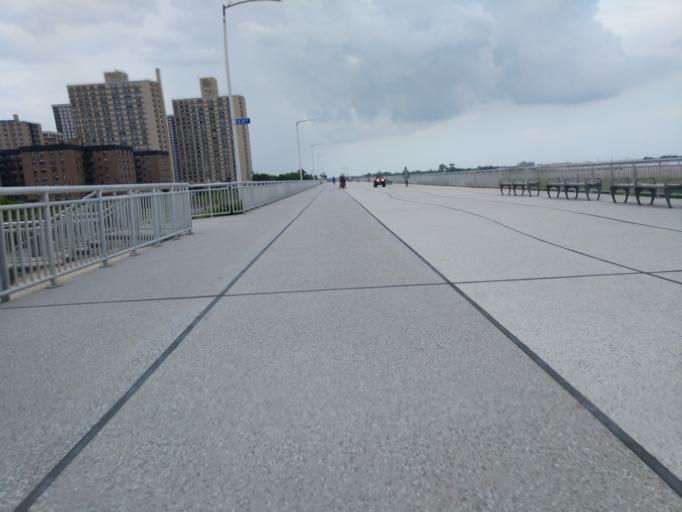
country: US
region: New York
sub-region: Nassau County
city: Atlantic Beach
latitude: 40.5924
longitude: -73.7577
